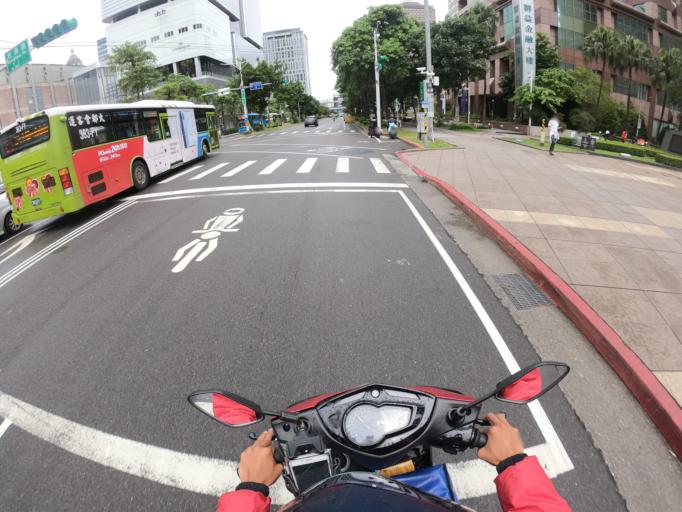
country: TW
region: Taipei
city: Taipei
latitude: 25.0355
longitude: 121.5685
